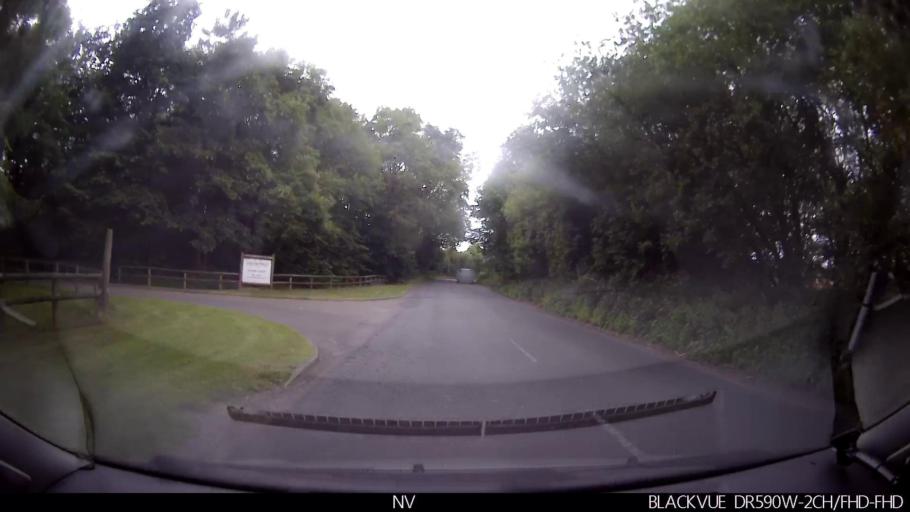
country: GB
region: England
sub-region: City of York
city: Holtby
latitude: 54.0455
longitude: -0.9590
